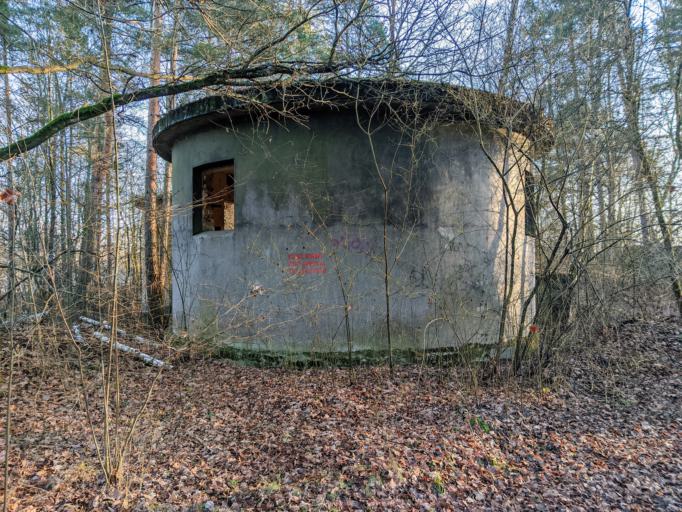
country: PL
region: Lubusz
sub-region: Powiat zielonogorski
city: Nowogrod Bobrzanski
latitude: 51.7772
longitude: 15.2404
